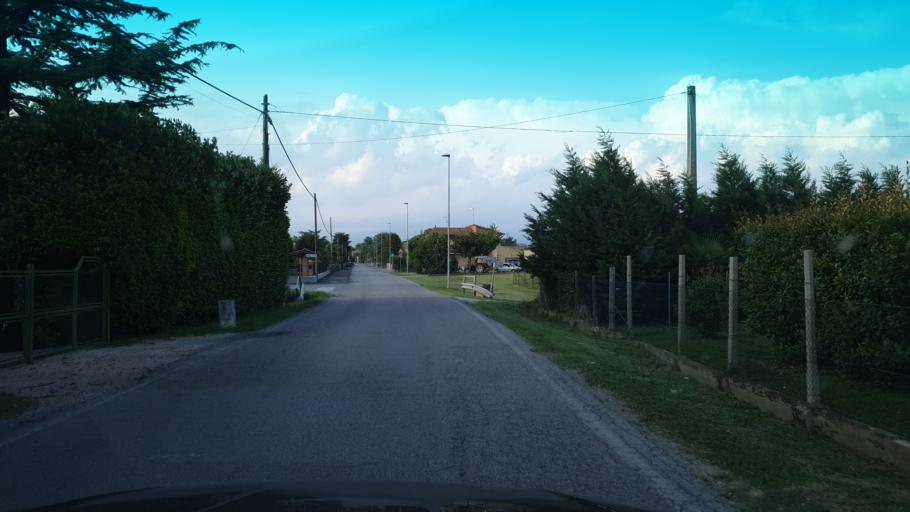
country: IT
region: Veneto
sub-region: Provincia di Rovigo
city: Castelguglielmo
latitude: 45.0183
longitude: 11.5343
